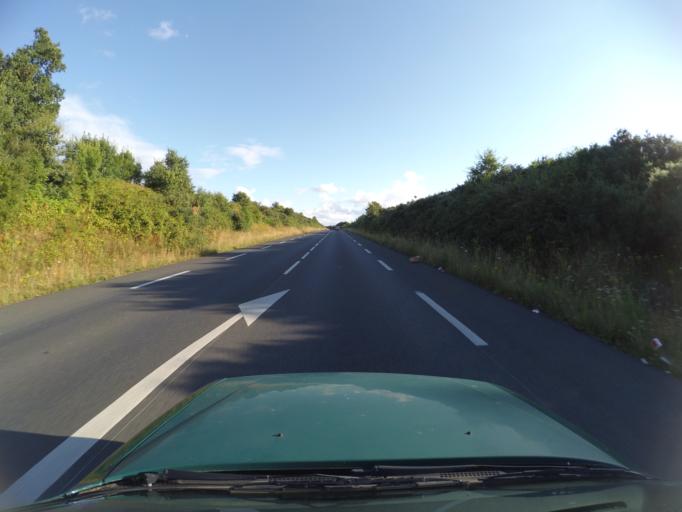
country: FR
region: Pays de la Loire
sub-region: Departement de la Vendee
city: Saint-Hilaire-de-Loulay
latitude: 46.9885
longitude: -1.3528
